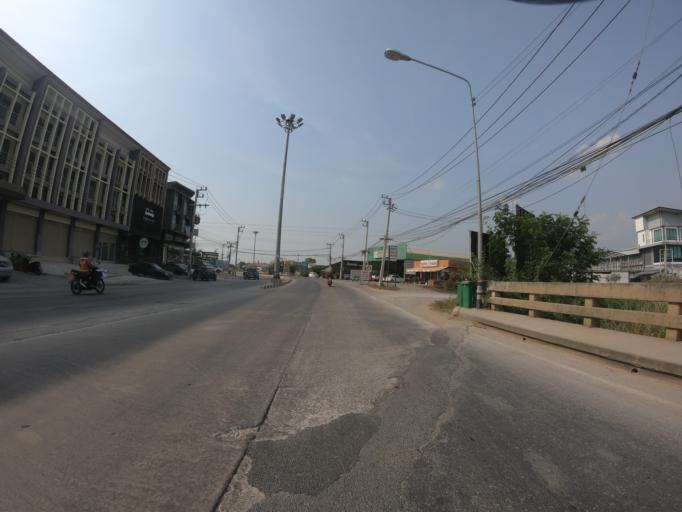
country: TH
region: Phra Nakhon Si Ayutthaya
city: Phra Nakhon Si Ayutthaya
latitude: 14.3395
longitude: 100.5966
